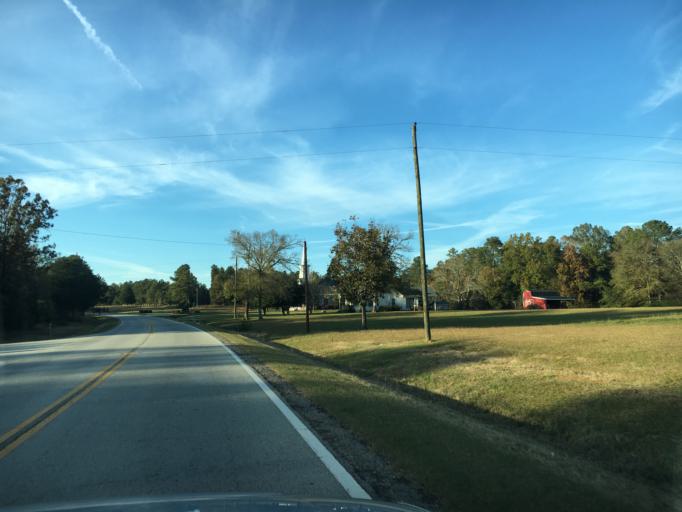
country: US
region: Georgia
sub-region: Elbert County
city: Elberton
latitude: 34.0137
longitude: -82.7814
